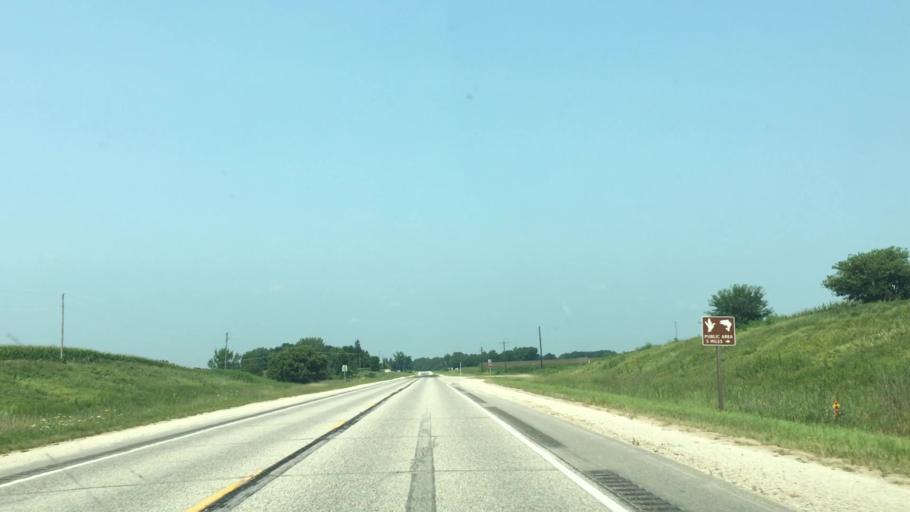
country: US
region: Iowa
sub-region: Fayette County
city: Fayette
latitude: 42.8165
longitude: -91.8051
